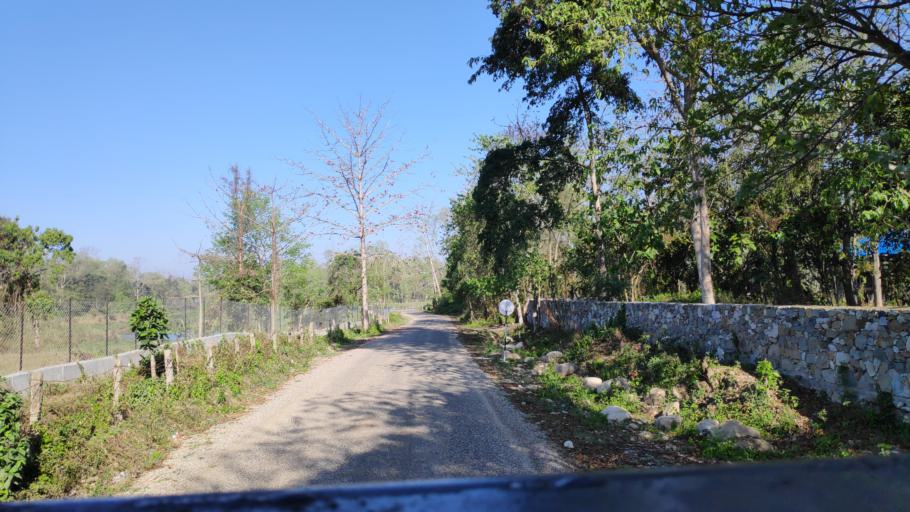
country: NP
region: Central Region
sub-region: Narayani Zone
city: Bharatpur
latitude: 27.5683
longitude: 84.5197
